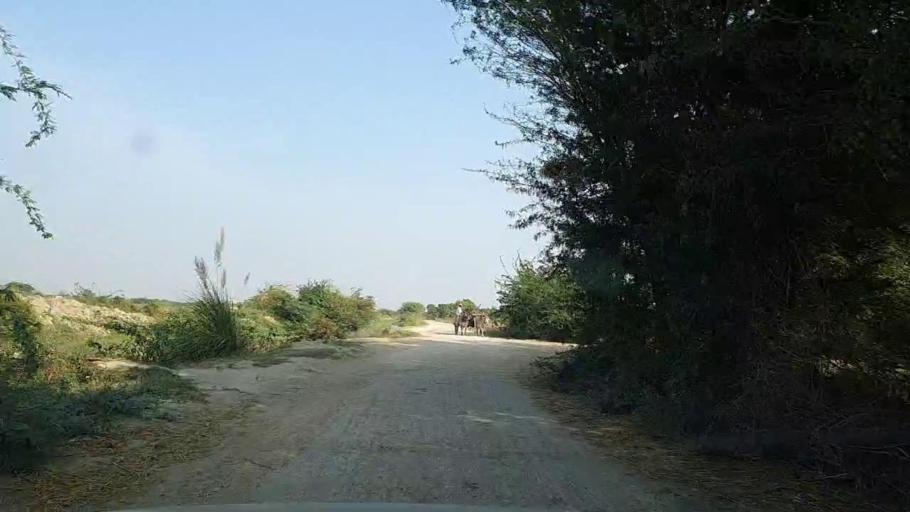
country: PK
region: Sindh
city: Mirpur Sakro
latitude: 24.5968
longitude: 67.5925
